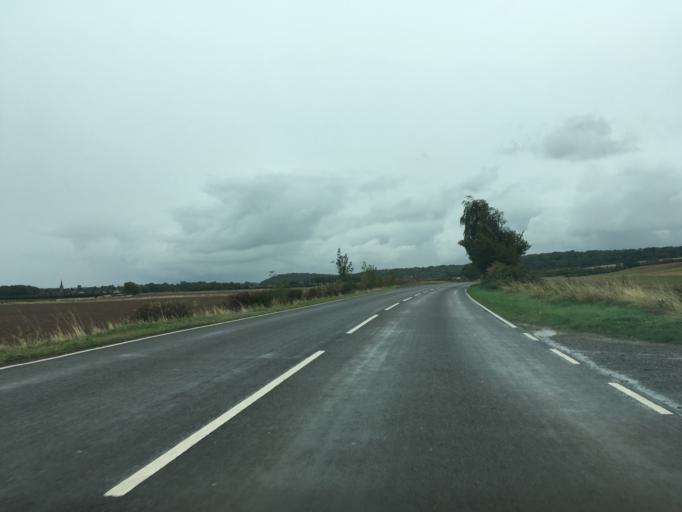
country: GB
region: England
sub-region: Nottinghamshire
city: Ruddington
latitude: 52.8574
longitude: -1.1562
